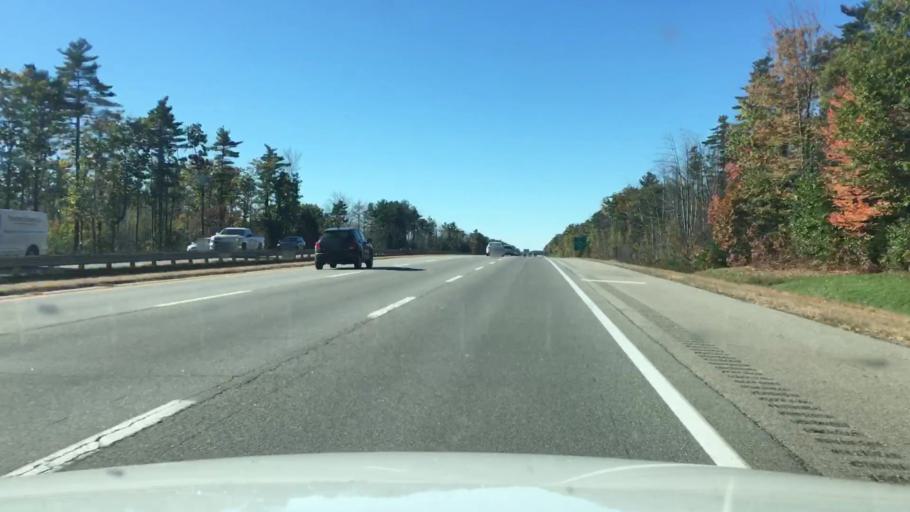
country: US
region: Maine
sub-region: York County
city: Saco
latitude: 43.5473
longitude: -70.4323
